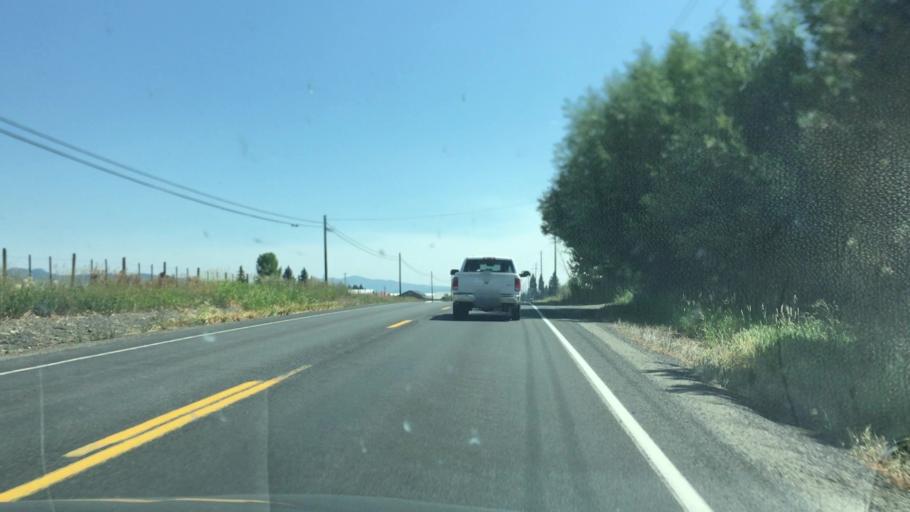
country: US
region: Idaho
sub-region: Valley County
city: McCall
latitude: 44.8424
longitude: -116.0880
